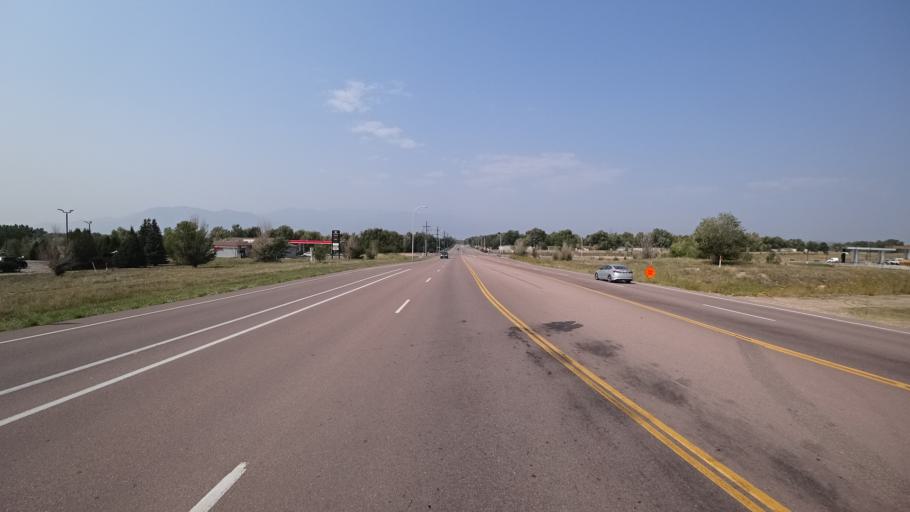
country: US
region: Colorado
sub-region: El Paso County
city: Cimarron Hills
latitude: 38.8248
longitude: -104.7272
